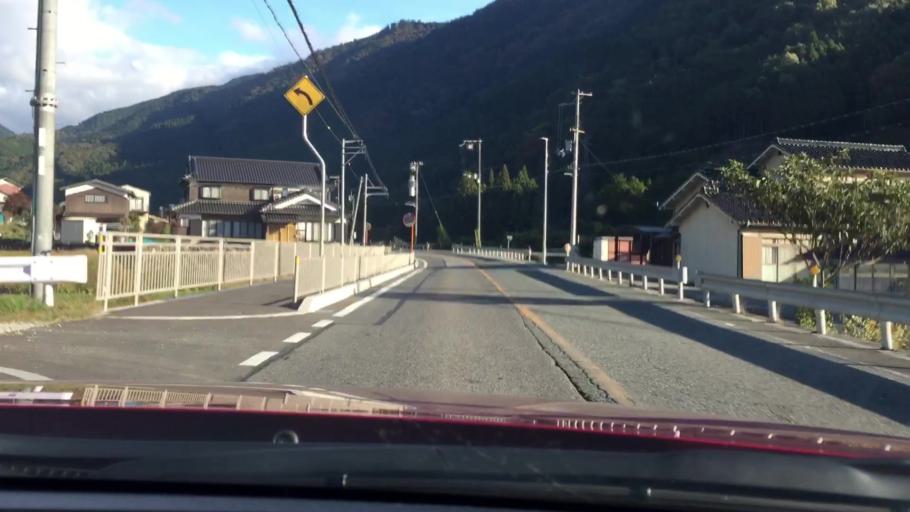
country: JP
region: Hyogo
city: Yamazakicho-nakabirose
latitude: 35.1198
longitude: 134.5688
